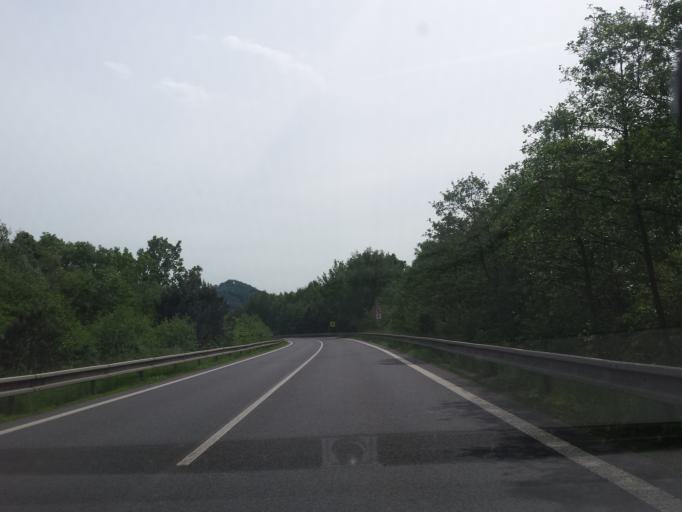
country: CZ
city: Novy Bor
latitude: 50.7584
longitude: 14.5346
